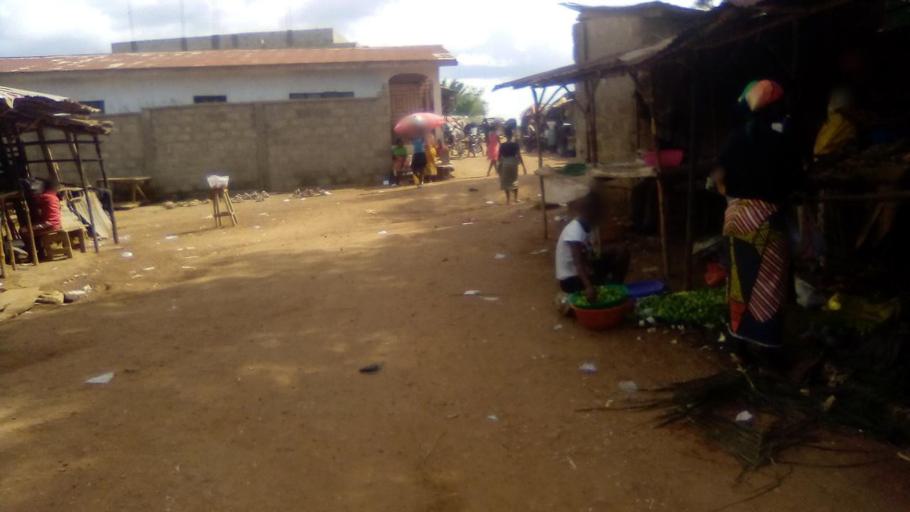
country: SL
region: Southern Province
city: Bo
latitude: 7.9520
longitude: -11.7202
